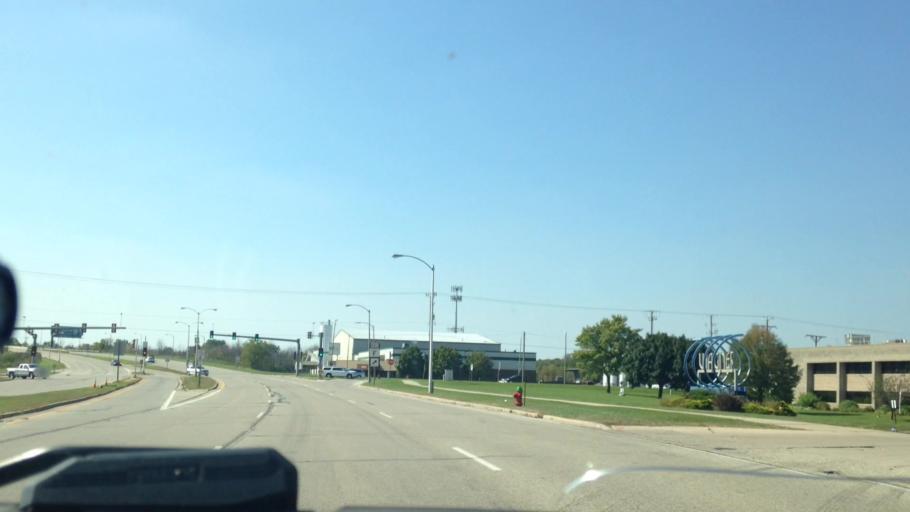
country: US
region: Wisconsin
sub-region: Waukesha County
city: Menomonee Falls
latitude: 43.1786
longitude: -88.0422
